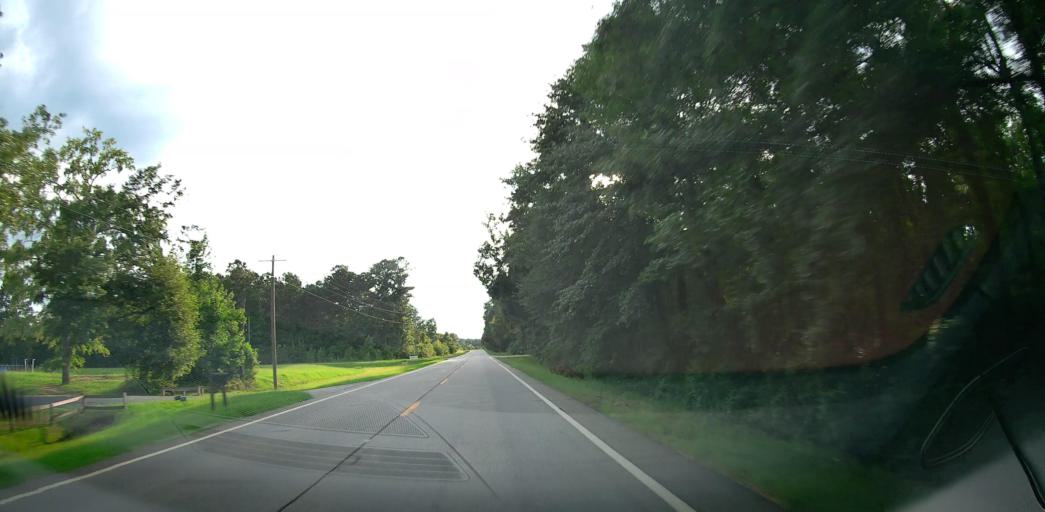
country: US
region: Georgia
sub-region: Pulaski County
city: Hawkinsville
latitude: 32.2955
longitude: -83.5514
